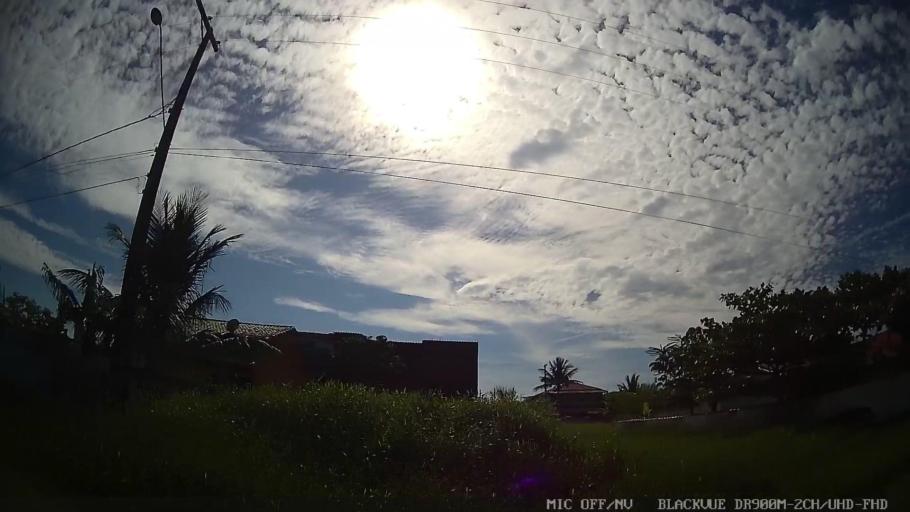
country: BR
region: Sao Paulo
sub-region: Iguape
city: Iguape
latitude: -24.7728
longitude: -47.5919
